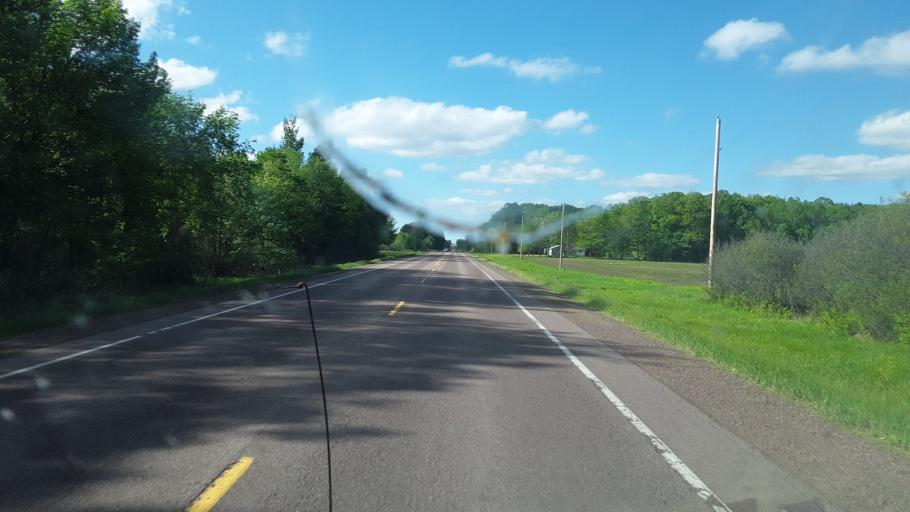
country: US
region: Wisconsin
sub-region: Wood County
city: Marshfield
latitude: 44.5165
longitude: -90.1799
